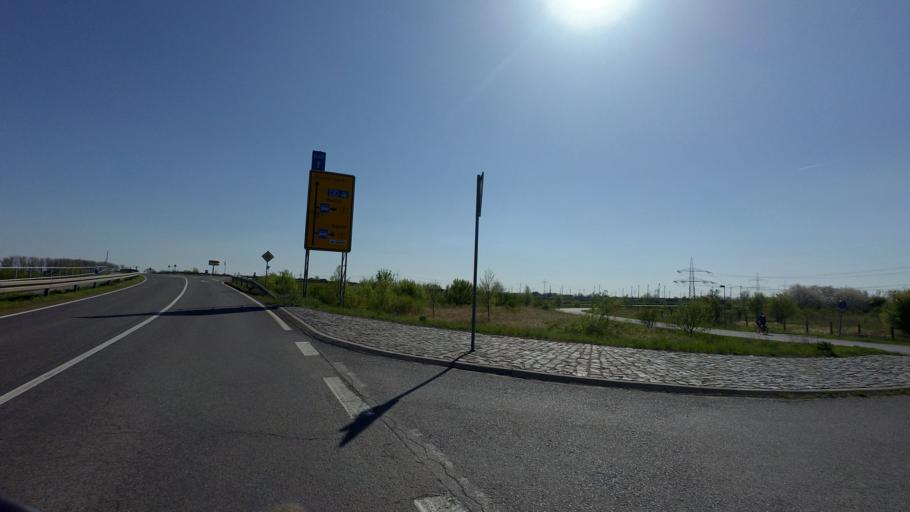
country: DE
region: Brandenburg
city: Wustermark
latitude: 52.5586
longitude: 12.9529
